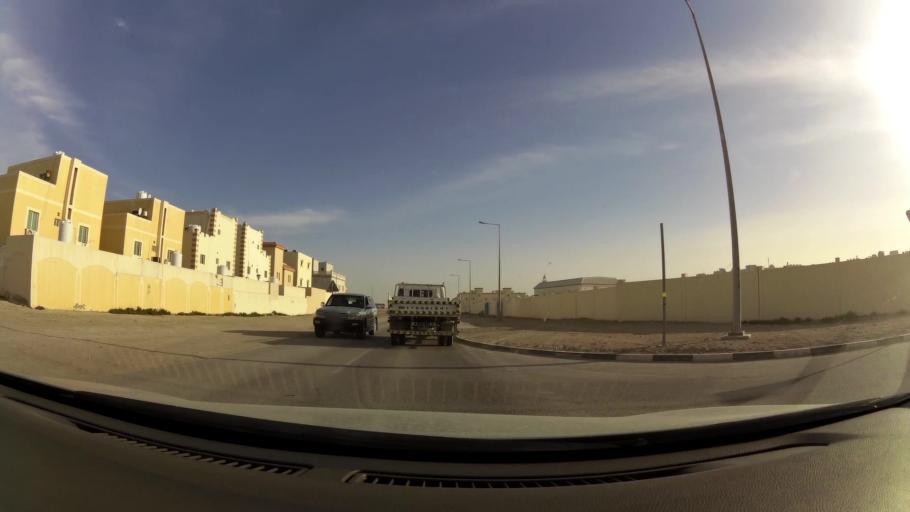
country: QA
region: Al Wakrah
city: Al Wakrah
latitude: 25.1458
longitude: 51.6059
